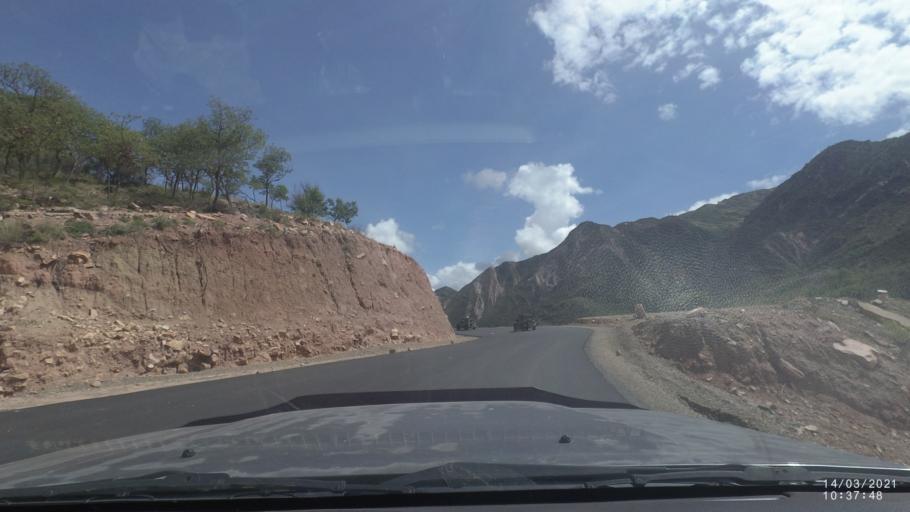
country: BO
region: Cochabamba
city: Cliza
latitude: -17.8974
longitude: -65.8897
